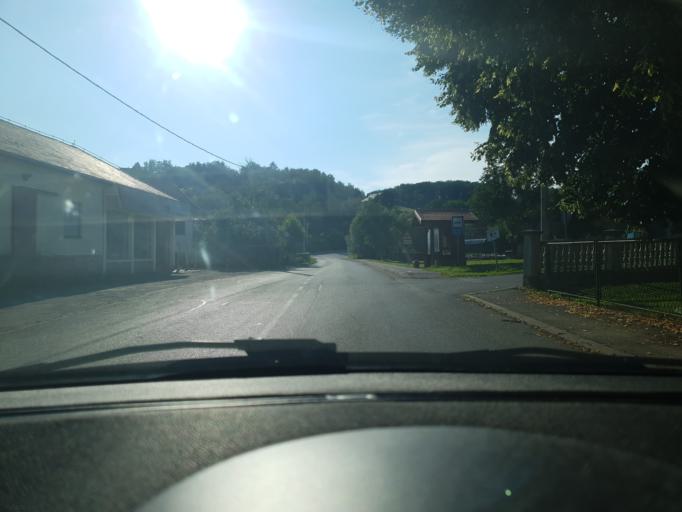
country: HR
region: Krapinsko-Zagorska
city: Radoboj
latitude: 46.1556
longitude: 15.9415
